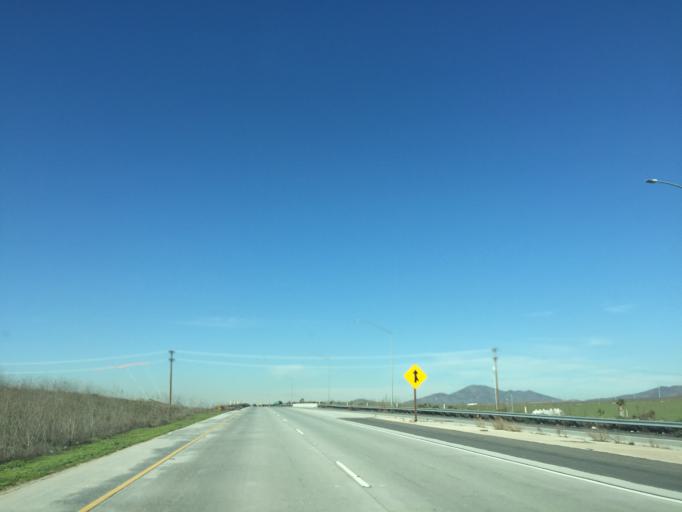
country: MX
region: Baja California
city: Tijuana
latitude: 32.5656
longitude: -116.9479
